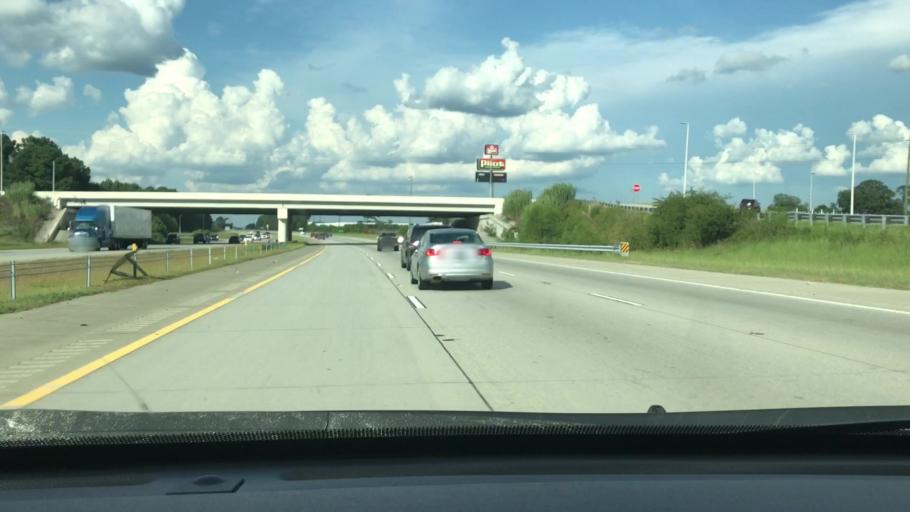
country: US
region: South Carolina
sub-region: Florence County
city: Florence
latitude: 34.2682
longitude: -79.7053
